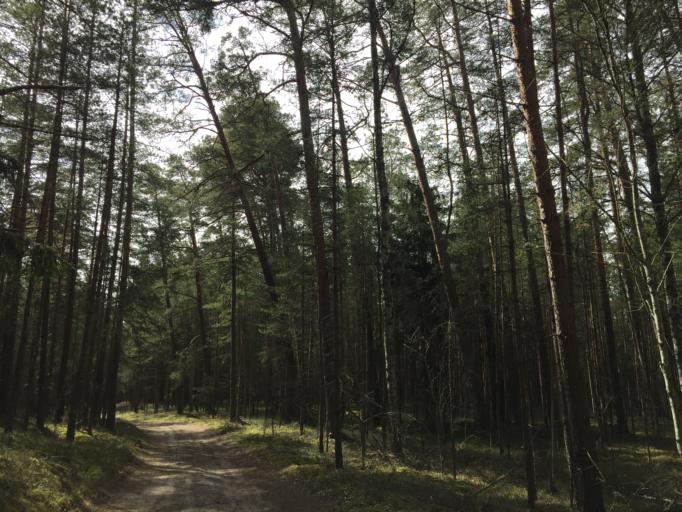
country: LV
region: Salacgrivas
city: Salacgriva
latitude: 57.6918
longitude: 24.3607
